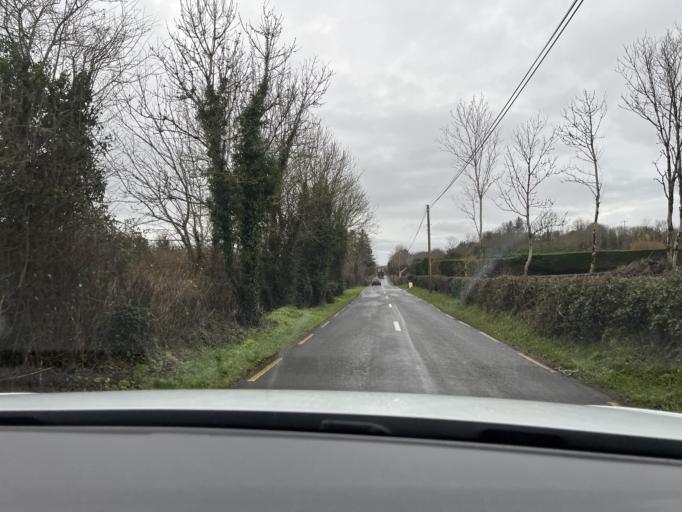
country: IE
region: Connaught
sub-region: County Leitrim
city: Manorhamilton
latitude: 54.2454
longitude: -8.2578
